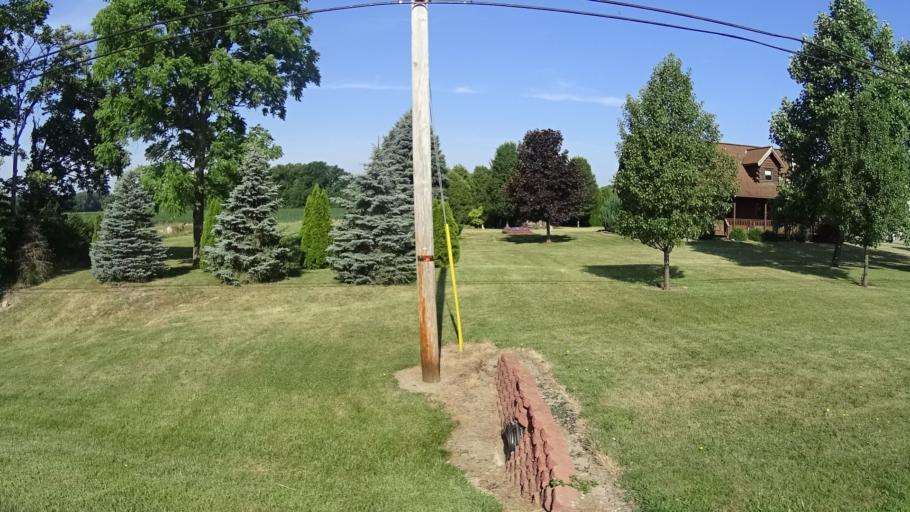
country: US
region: Ohio
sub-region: Erie County
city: Sandusky
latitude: 41.4330
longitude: -82.8236
